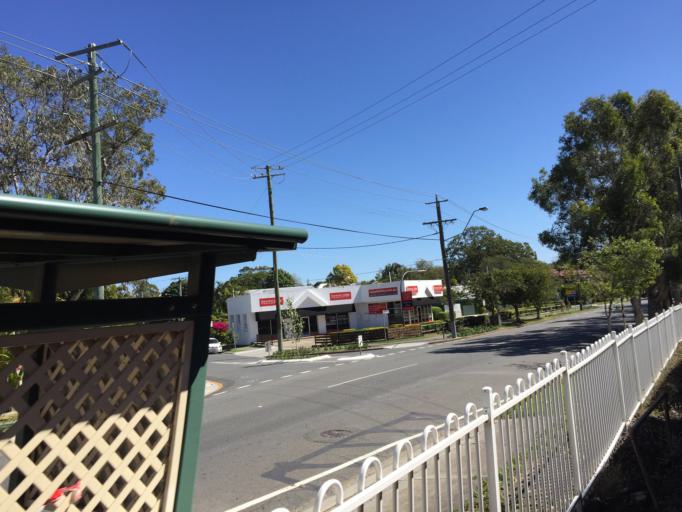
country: AU
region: Queensland
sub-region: Brisbane
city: Taringa
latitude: -27.5205
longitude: 152.9758
